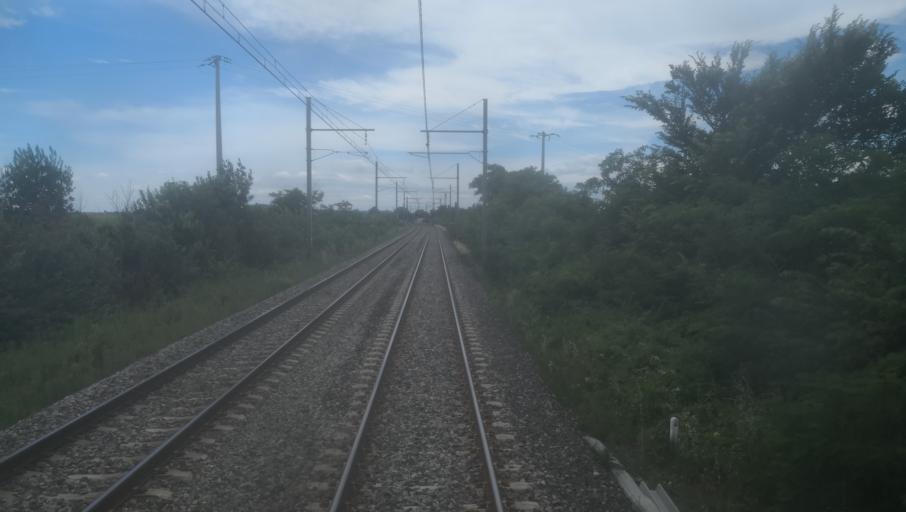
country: FR
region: Languedoc-Roussillon
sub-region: Departement de l'Herault
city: Colombiers
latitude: 43.3319
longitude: 3.1676
